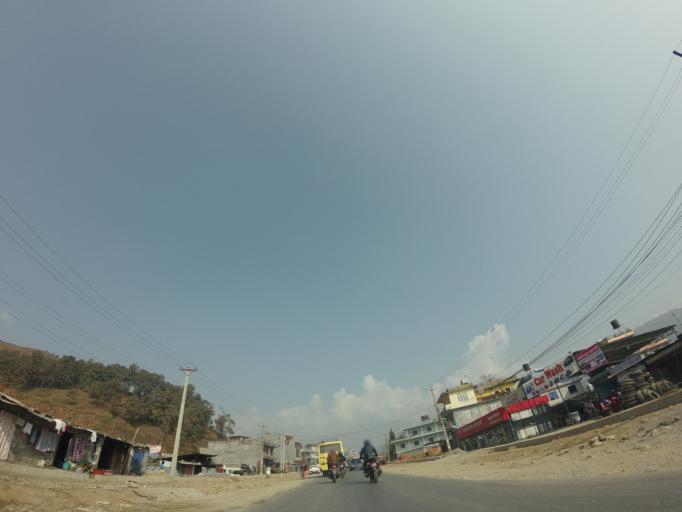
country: NP
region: Western Region
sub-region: Gandaki Zone
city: Pokhara
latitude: 28.2269
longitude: 83.9809
